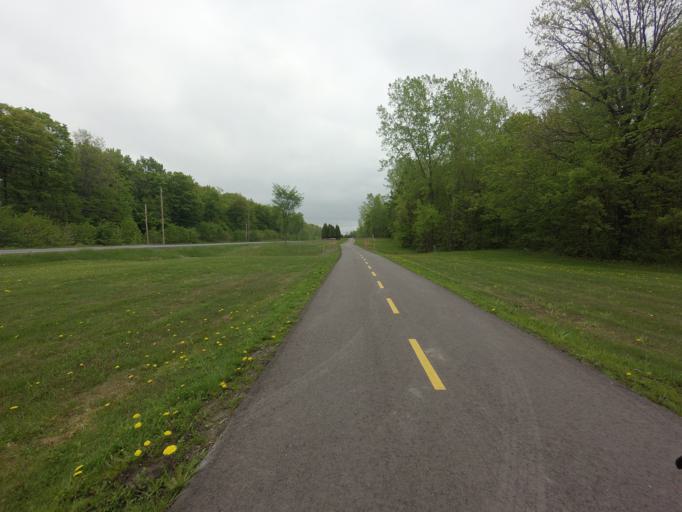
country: CA
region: Ontario
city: Cornwall
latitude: 45.0331
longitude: -74.8218
